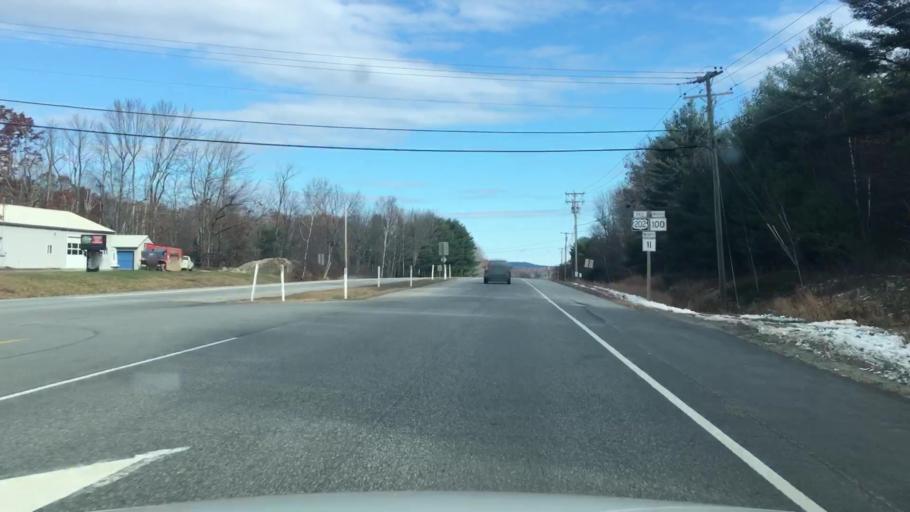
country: US
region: Maine
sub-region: Kennebec County
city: Winthrop
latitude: 44.3080
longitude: -69.9542
